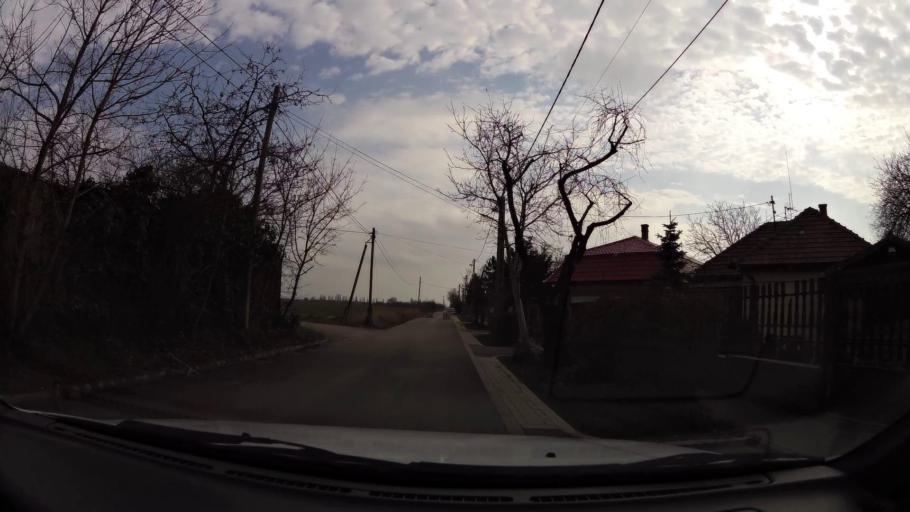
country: HU
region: Pest
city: Csomor
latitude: 47.5290
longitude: 19.2365
